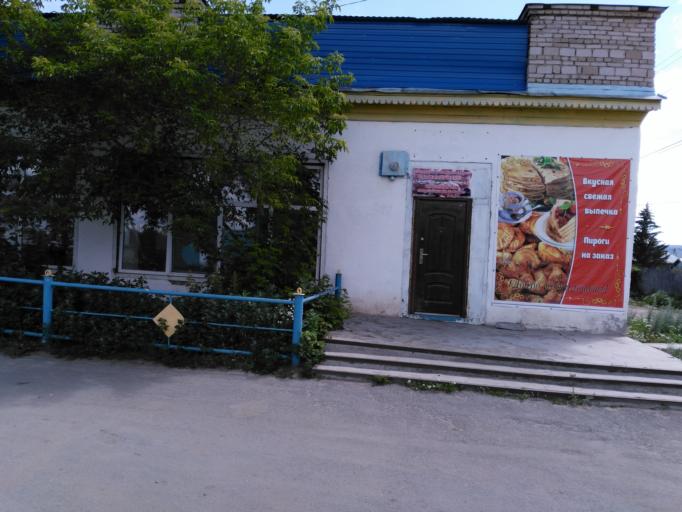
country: RU
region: Bashkortostan
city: Akhunovo
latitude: 54.2071
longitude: 59.5985
